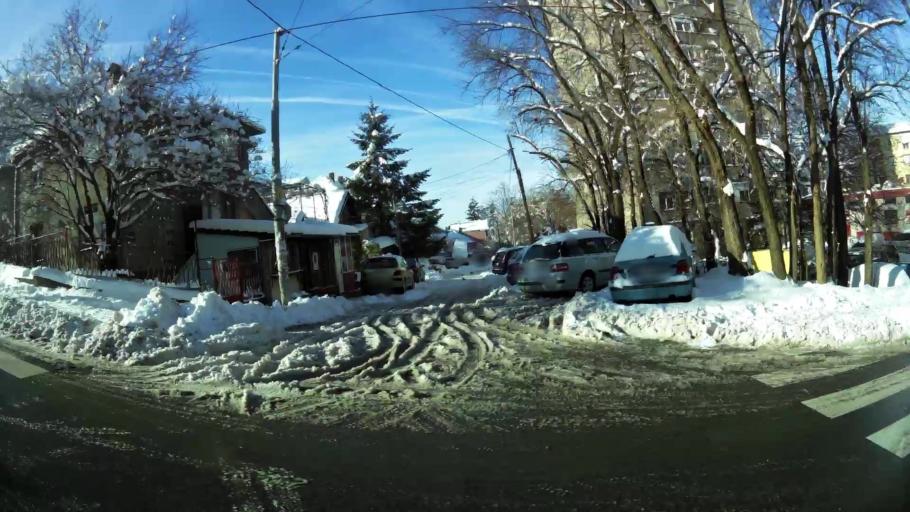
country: RS
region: Central Serbia
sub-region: Belgrade
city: Palilula
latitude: 44.7861
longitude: 20.5062
